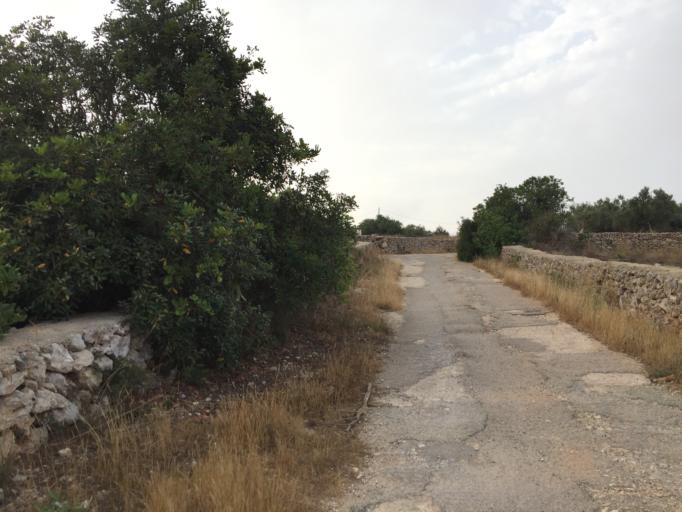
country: MT
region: L-Imgarr
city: Imgarr
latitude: 35.9335
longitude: 14.3860
